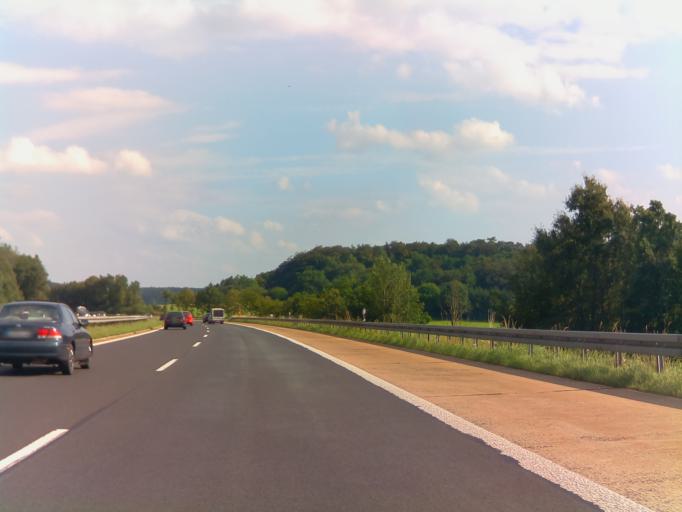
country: DE
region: Bavaria
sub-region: Regierungsbezirk Unterfranken
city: Schondra
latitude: 50.2849
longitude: 9.8568
